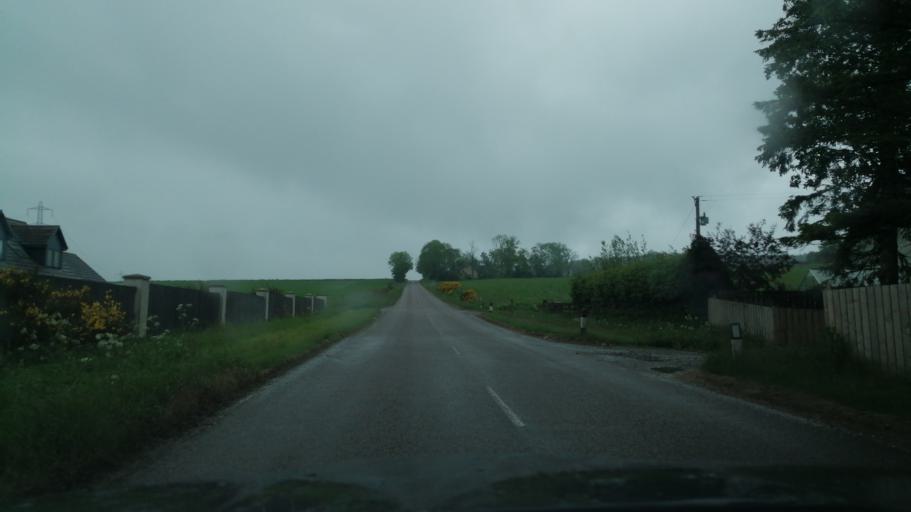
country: GB
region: Scotland
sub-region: Aberdeenshire
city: Huntly
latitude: 57.5451
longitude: -2.8093
